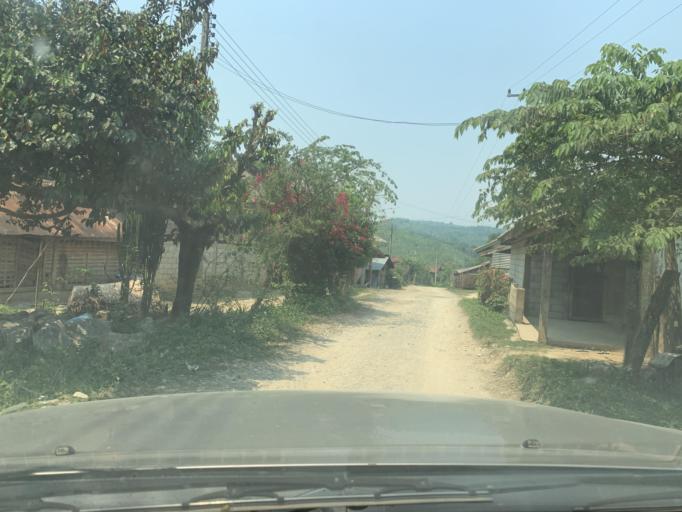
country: LA
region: Louangphabang
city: Louangphabang
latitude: 19.8806
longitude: 102.2619
